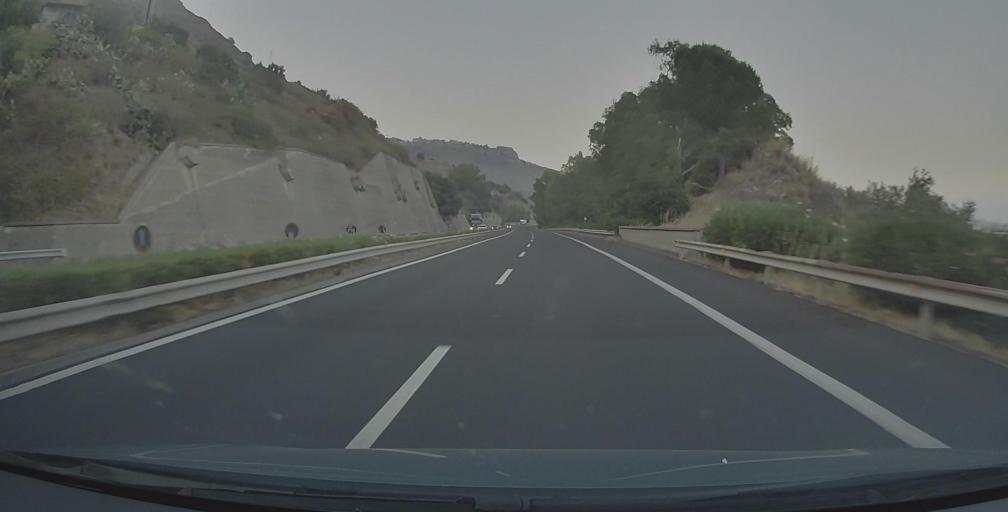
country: IT
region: Sicily
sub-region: Messina
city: Letojanni
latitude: 37.8949
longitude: 15.3223
